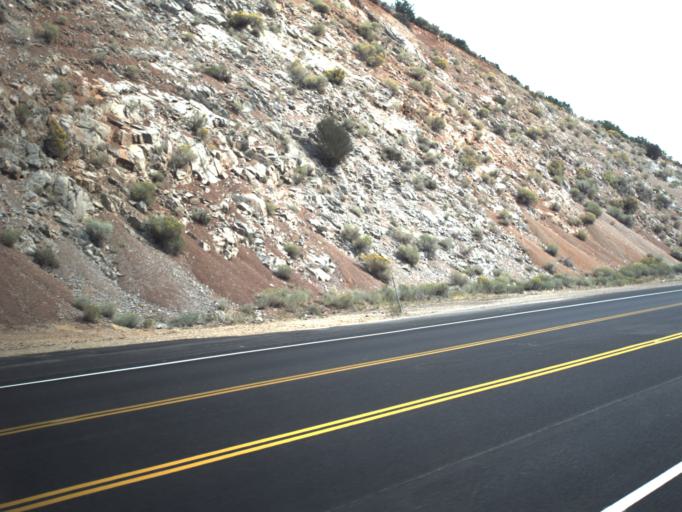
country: US
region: Utah
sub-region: Summit County
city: Park City
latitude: 40.6407
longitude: -111.3974
